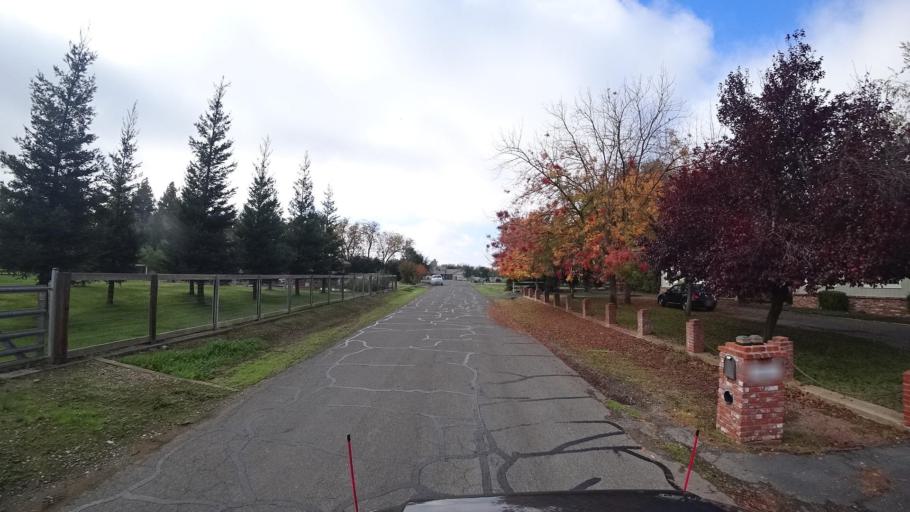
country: US
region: California
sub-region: Sacramento County
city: Vineyard
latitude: 38.4331
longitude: -121.3280
